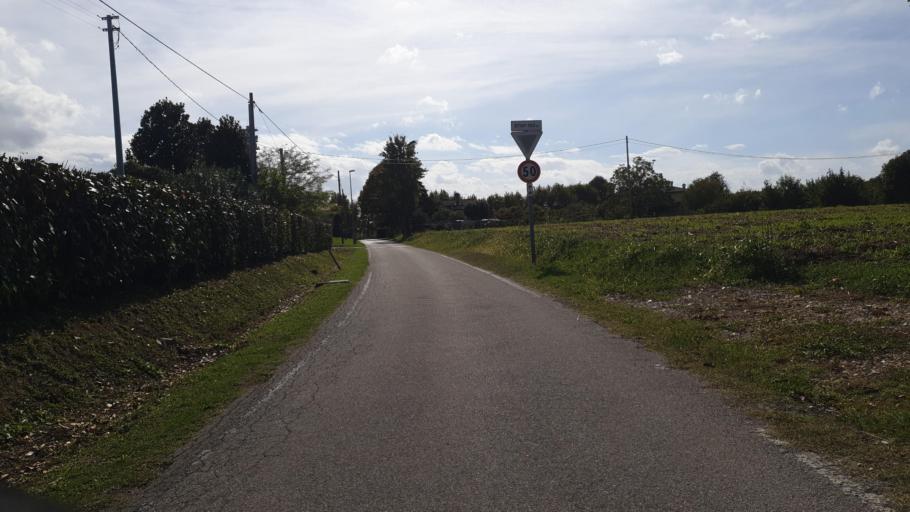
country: IT
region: Veneto
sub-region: Provincia di Padova
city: Arzergrande
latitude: 45.2782
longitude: 12.0548
